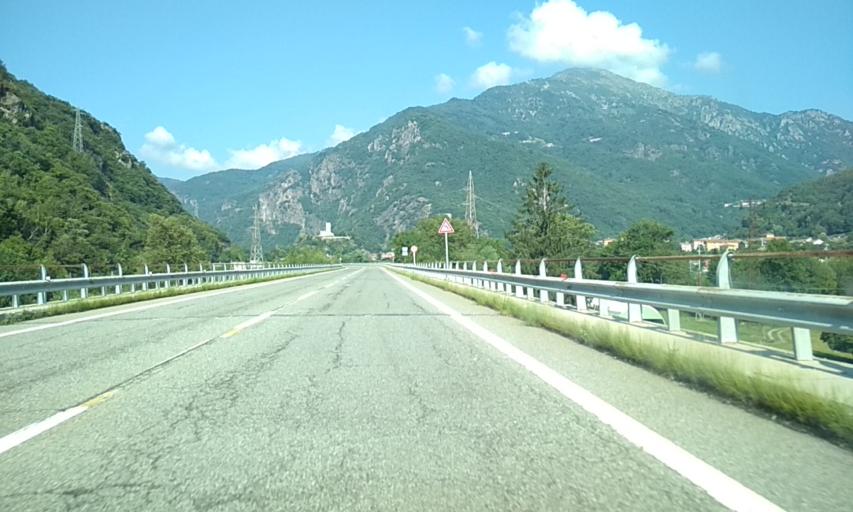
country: IT
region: Piedmont
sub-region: Provincia di Torino
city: Pont-Canavese
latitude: 45.4162
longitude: 7.6106
